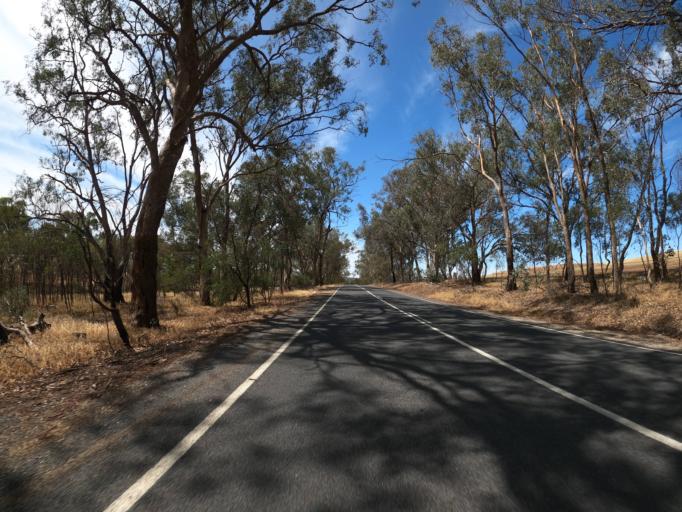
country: AU
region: Victoria
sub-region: Benalla
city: Benalla
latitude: -36.3821
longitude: 145.9778
